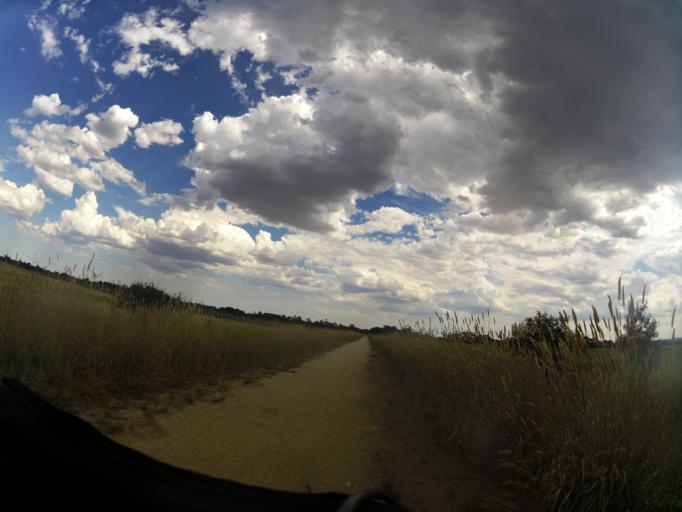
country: AU
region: Victoria
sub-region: Wellington
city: Heyfield
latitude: -38.0022
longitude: 146.6979
